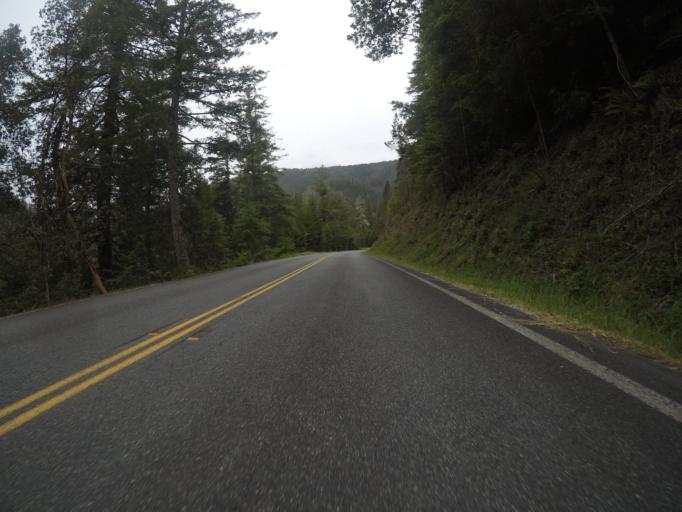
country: US
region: California
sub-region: Del Norte County
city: Bertsch-Oceanview
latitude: 41.7647
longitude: -124.0050
